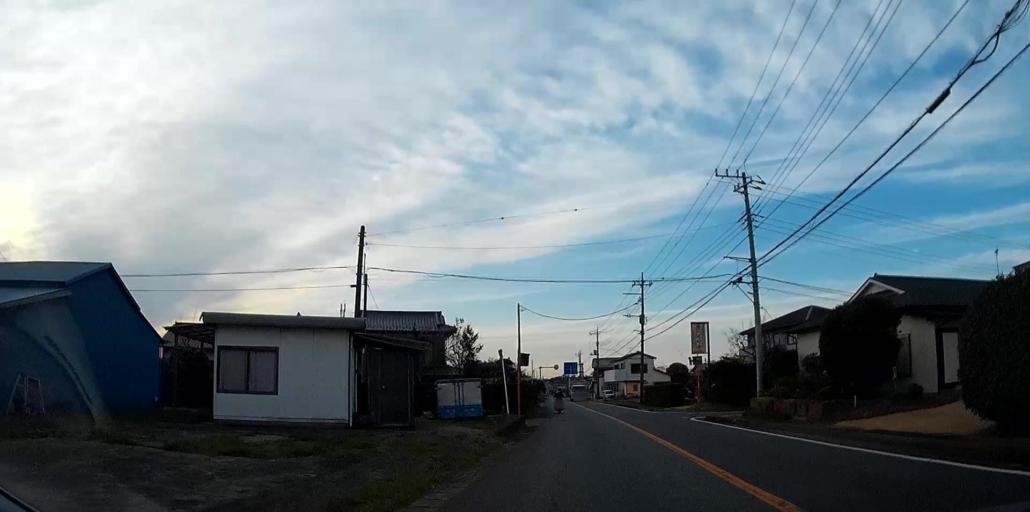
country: JP
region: Chiba
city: Ichihara
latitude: 35.3880
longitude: 140.0602
